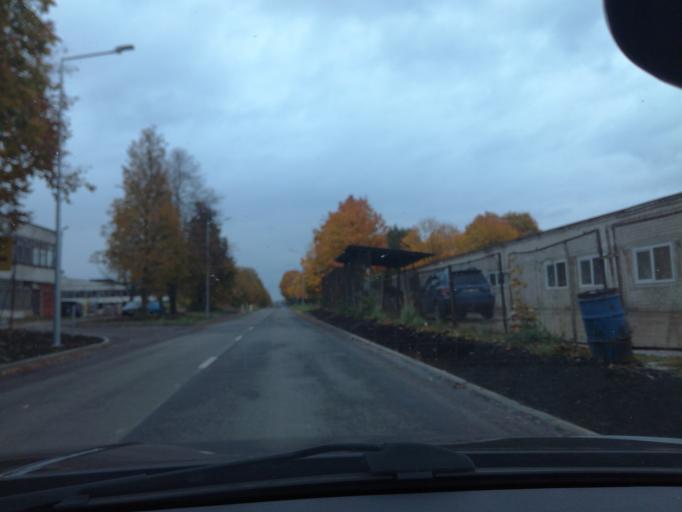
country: LT
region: Alytaus apskritis
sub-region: Alytus
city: Alytus
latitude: 54.4186
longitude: 24.0150
